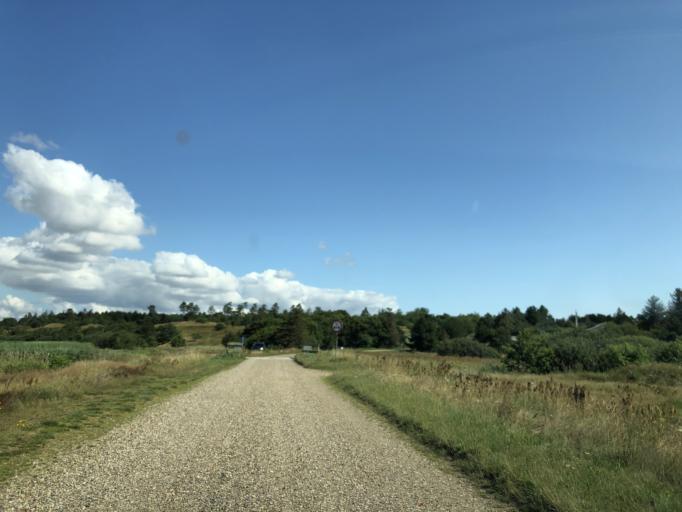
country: DK
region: Central Jutland
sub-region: Skive Kommune
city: Skive
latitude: 56.5202
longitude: 8.9567
